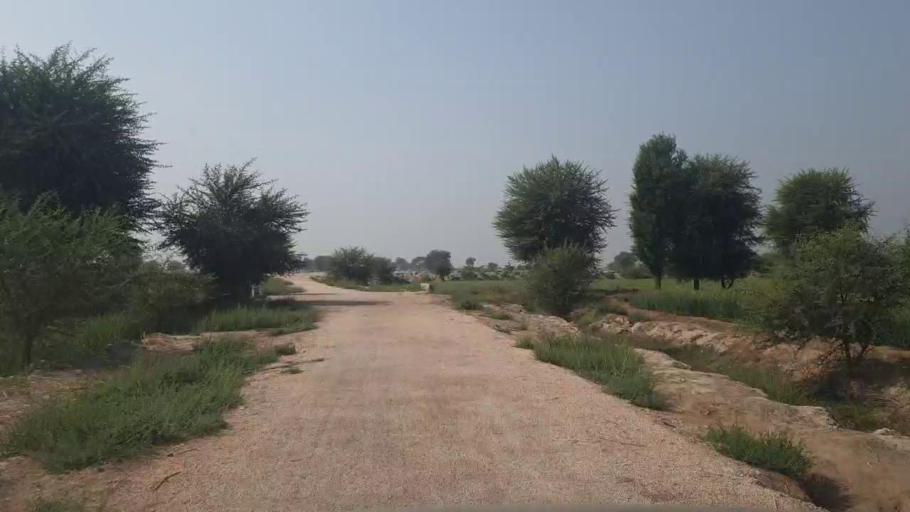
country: PK
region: Sindh
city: Umarkot
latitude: 25.4163
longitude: 69.6750
